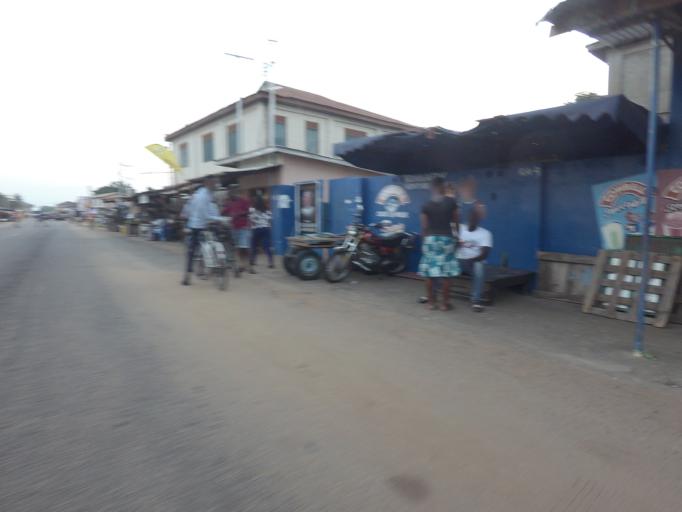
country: GH
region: Volta
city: Keta
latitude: 5.8916
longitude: 0.9849
